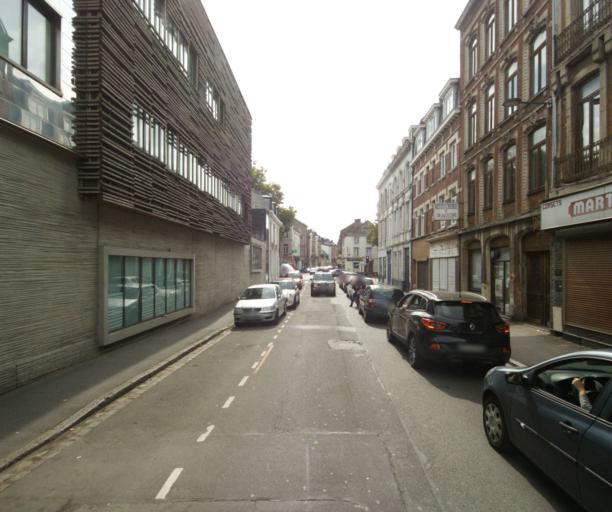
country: FR
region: Nord-Pas-de-Calais
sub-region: Departement du Nord
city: Lille
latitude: 50.6243
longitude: 3.0438
